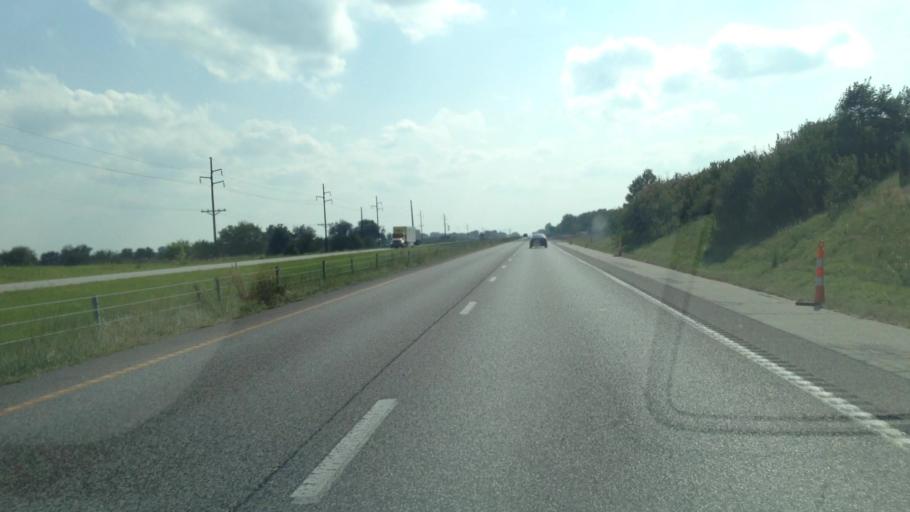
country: US
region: Missouri
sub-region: Clay County
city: Kearney
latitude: 39.3227
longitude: -94.3968
